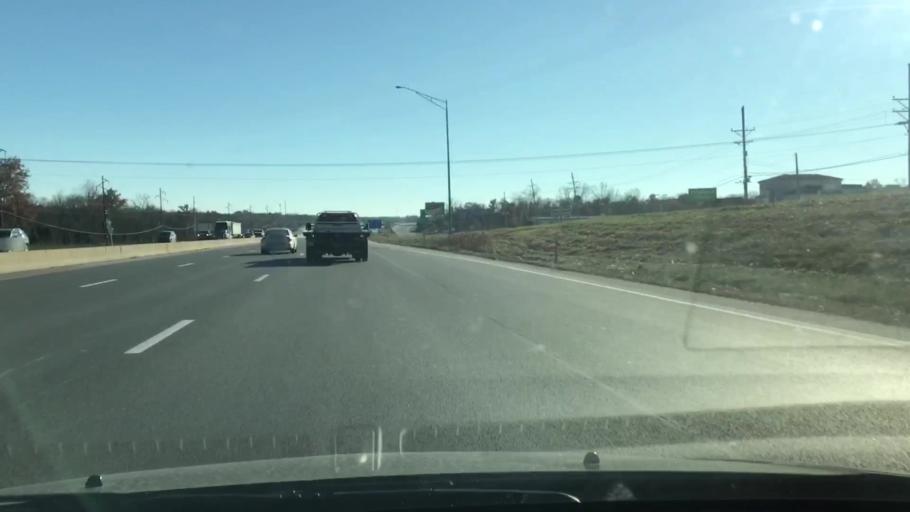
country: US
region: Missouri
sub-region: Jackson County
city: Grandview
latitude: 38.8663
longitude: -94.5269
